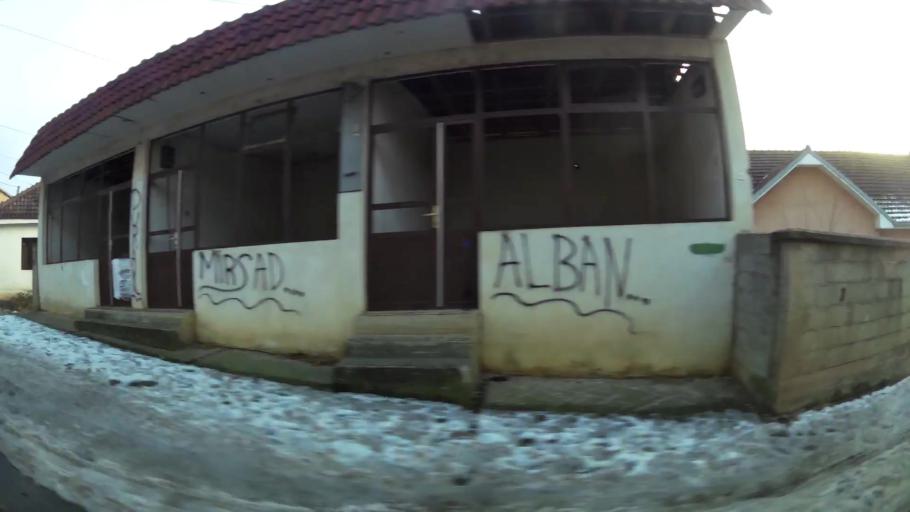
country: MK
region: Aracinovo
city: Arachinovo
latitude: 42.0272
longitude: 21.5615
